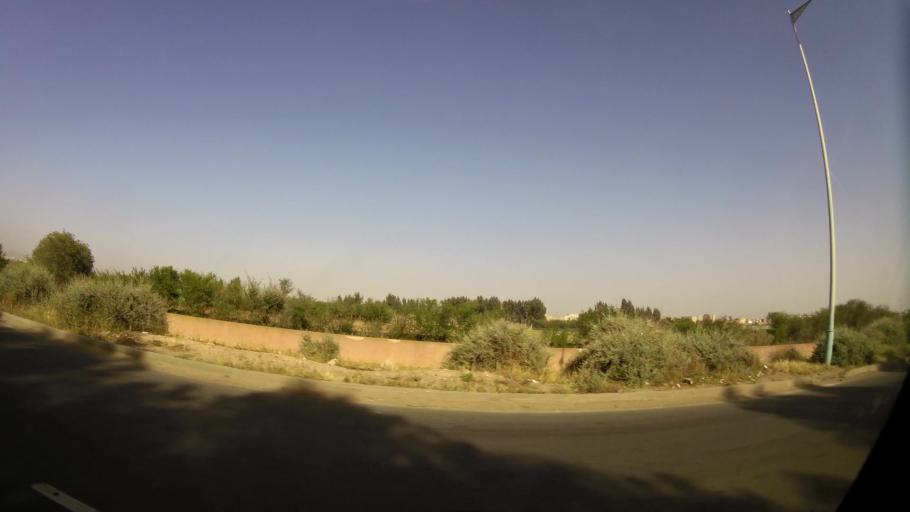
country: MA
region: Souss-Massa-Draa
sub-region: Inezgane-Ait Mellou
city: Inezgane
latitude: 30.3551
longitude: -9.5059
